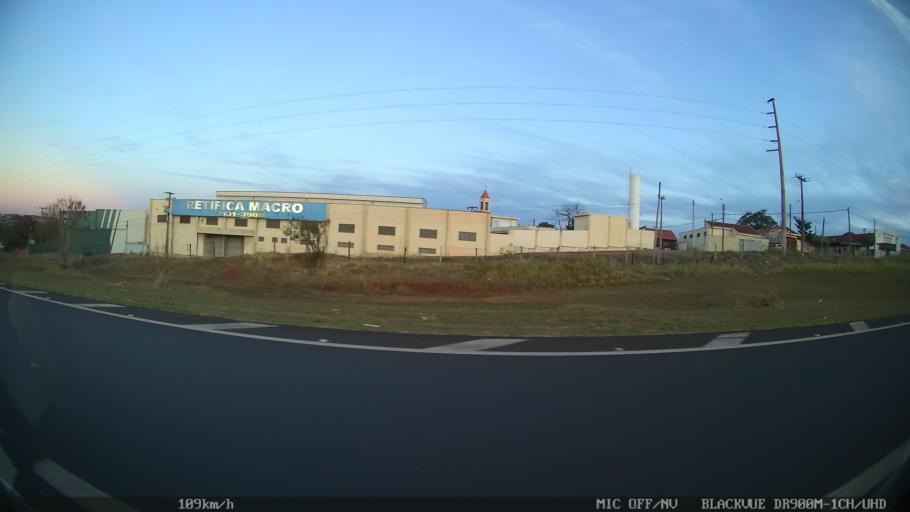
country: BR
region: Sao Paulo
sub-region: Catanduva
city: Catanduva
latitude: -21.1231
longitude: -48.9955
